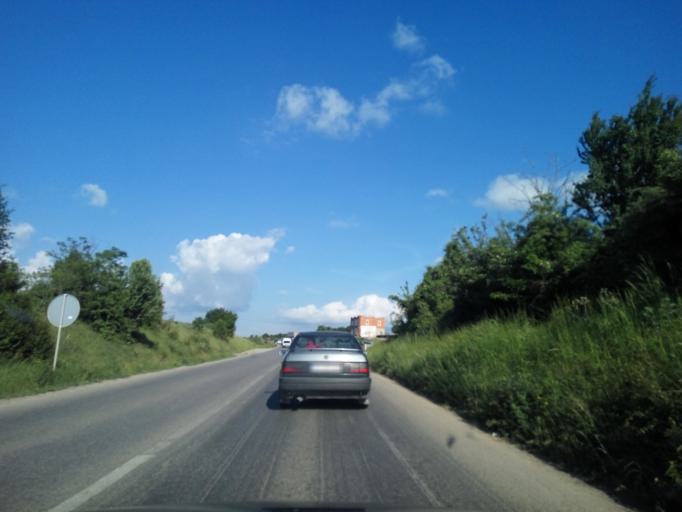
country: XK
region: Prizren
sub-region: Komuna e Malisheves
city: Llazice
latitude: 42.5878
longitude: 20.6729
